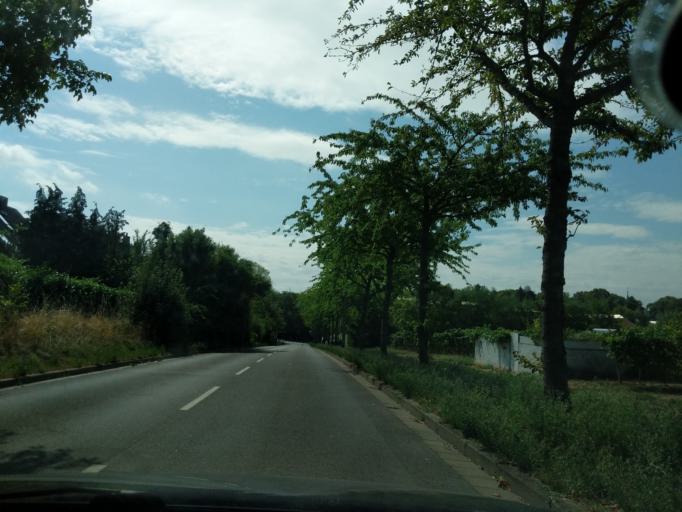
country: DE
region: Rheinland-Pfalz
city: Mainz
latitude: 49.9649
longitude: 8.2845
